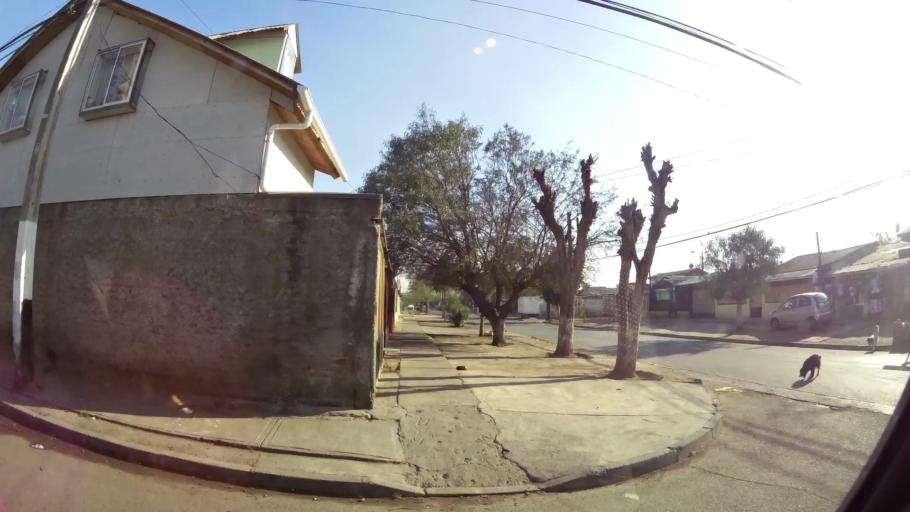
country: CL
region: Santiago Metropolitan
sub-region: Provincia de Santiago
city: Lo Prado
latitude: -33.4407
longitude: -70.7450
